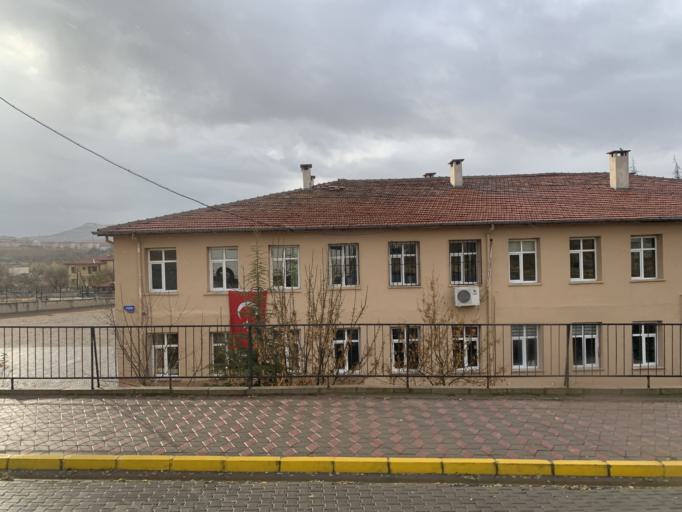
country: TR
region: Nevsehir
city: Avanos
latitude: 38.7205
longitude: 34.8559
